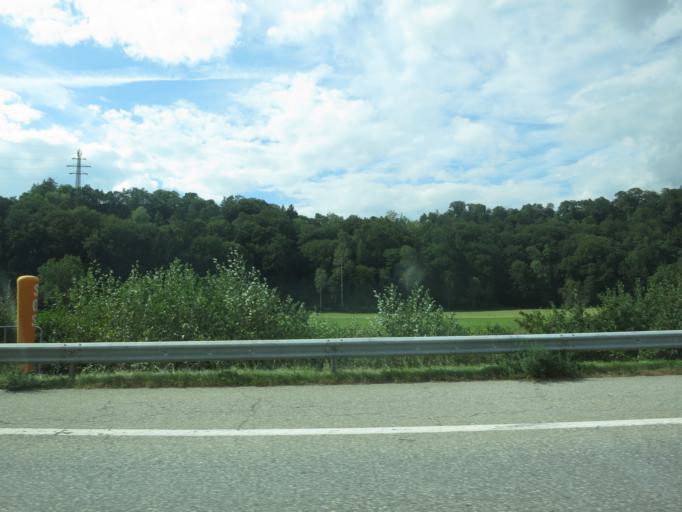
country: CH
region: Grisons
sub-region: Imboden District
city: Bonaduz
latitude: 46.8177
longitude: 9.4057
